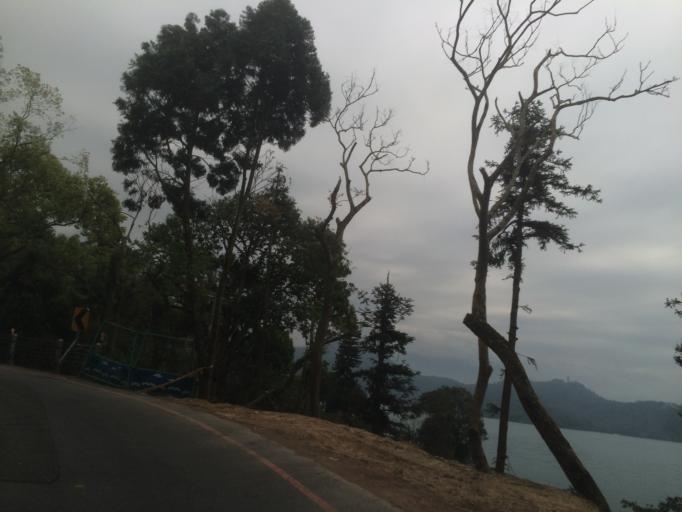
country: TW
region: Taiwan
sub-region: Nantou
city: Puli
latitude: 23.8708
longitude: 120.9226
